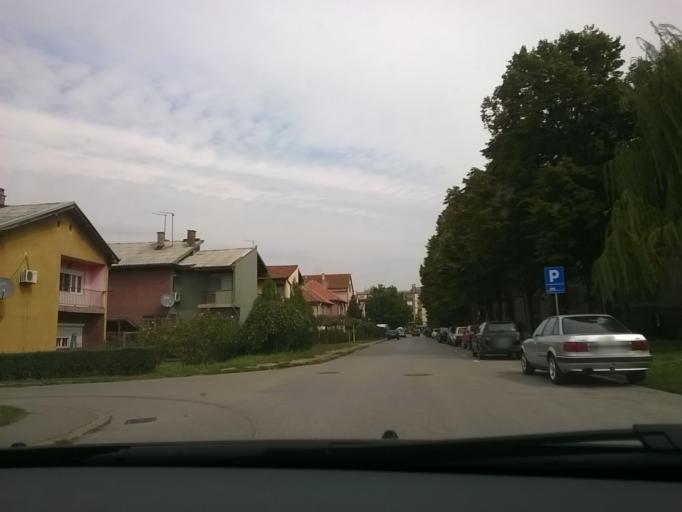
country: RS
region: Autonomna Pokrajina Vojvodina
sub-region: Juznobanatski Okrug
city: Pancevo
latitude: 44.8791
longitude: 20.6508
